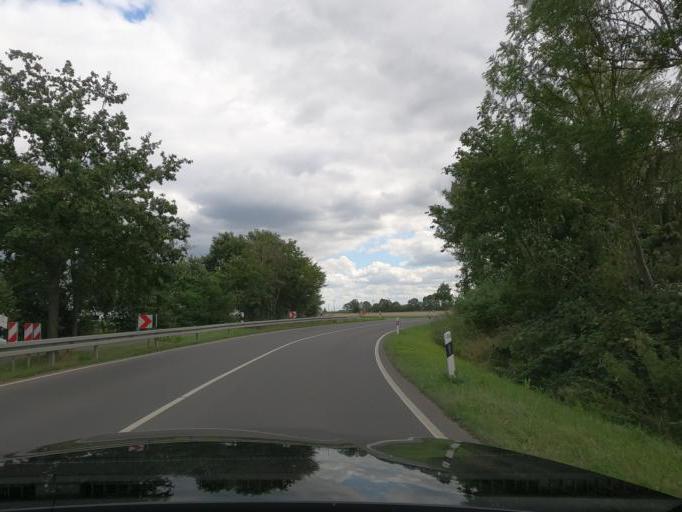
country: DE
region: Lower Saxony
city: Sehnde
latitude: 52.3165
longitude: 10.0275
